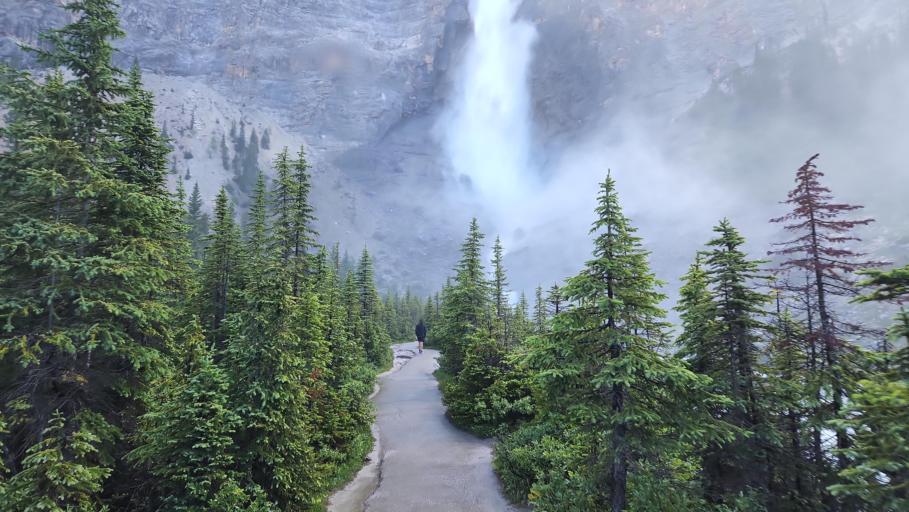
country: CA
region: Alberta
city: Lake Louise
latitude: 51.4979
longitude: -116.4790
